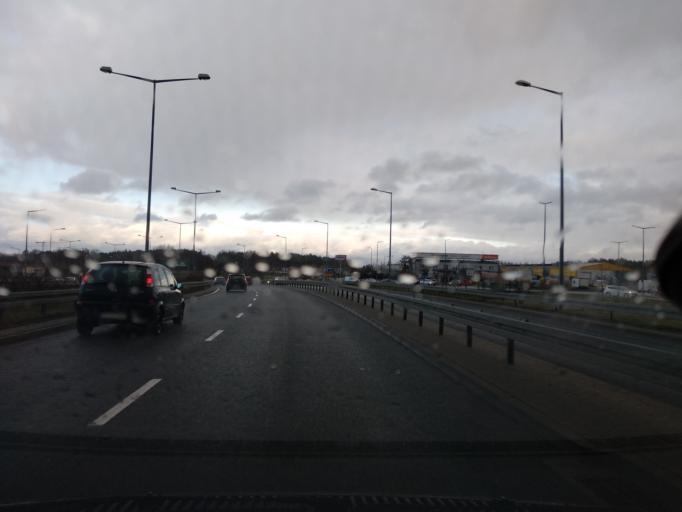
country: PL
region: Greater Poland Voivodeship
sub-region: Powiat koninski
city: Stare Miasto
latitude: 52.1853
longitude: 18.2282
